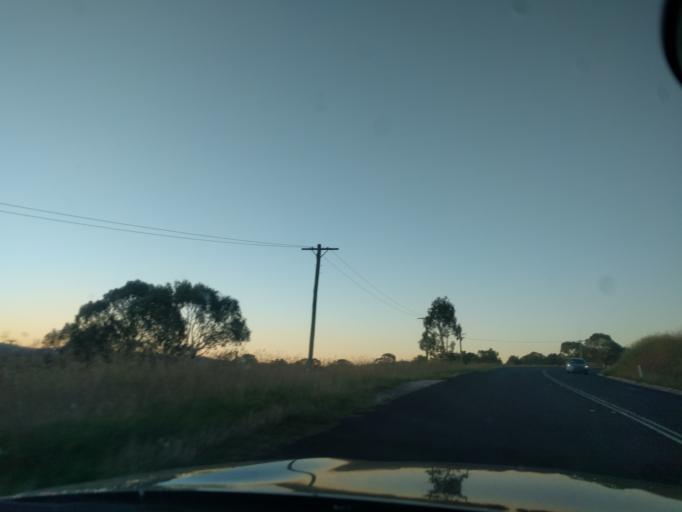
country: AU
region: New South Wales
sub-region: Armidale Dumaresq
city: Armidale
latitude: -30.5040
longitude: 151.6616
